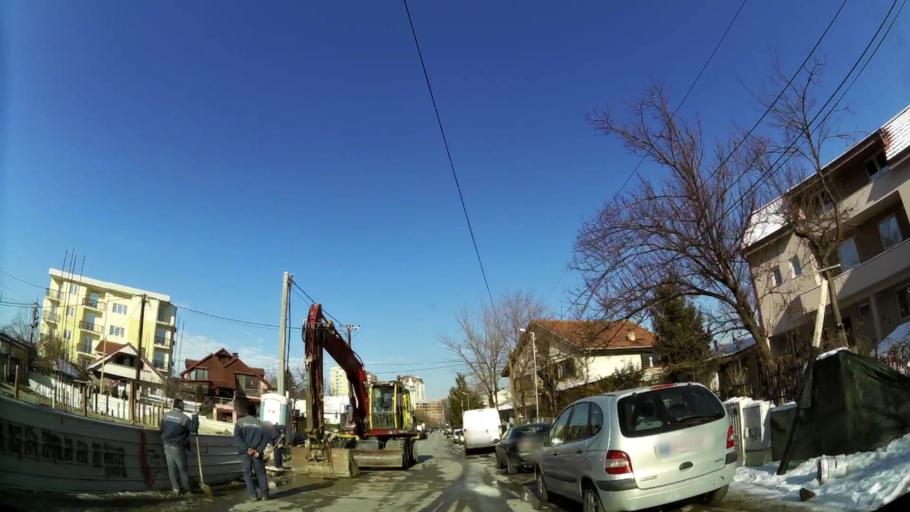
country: MK
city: Krushopek
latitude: 42.0011
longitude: 21.3793
